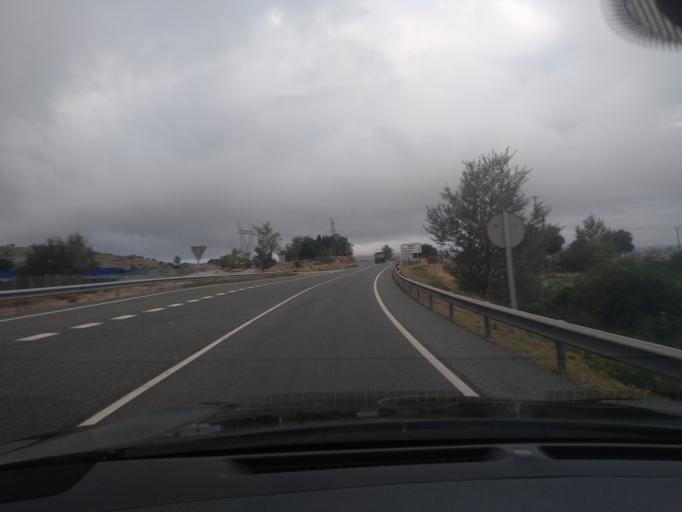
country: ES
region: Castille and Leon
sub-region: Provincia de Segovia
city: Otero de Herreros
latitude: 40.8060
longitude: -4.2073
